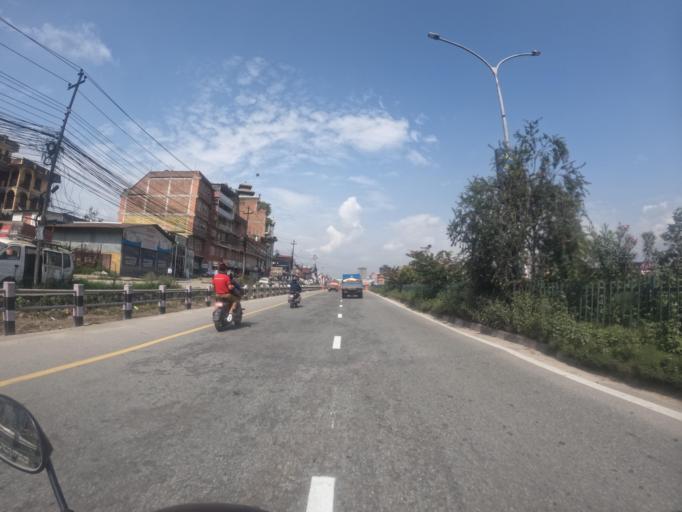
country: NP
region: Central Region
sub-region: Bagmati Zone
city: Bhaktapur
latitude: 27.6723
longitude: 85.4064
